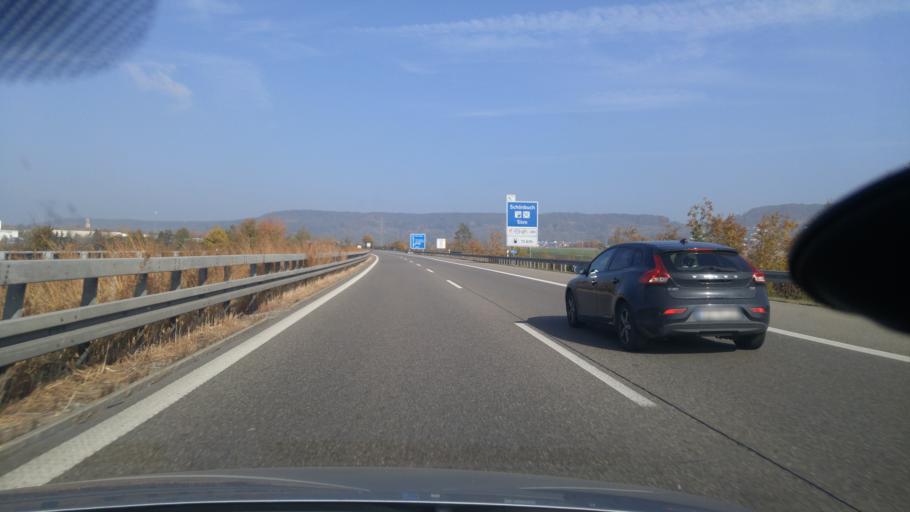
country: DE
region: Baden-Wuerttemberg
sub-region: Regierungsbezirk Stuttgart
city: Herrenberg
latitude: 48.5687
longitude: 8.8986
